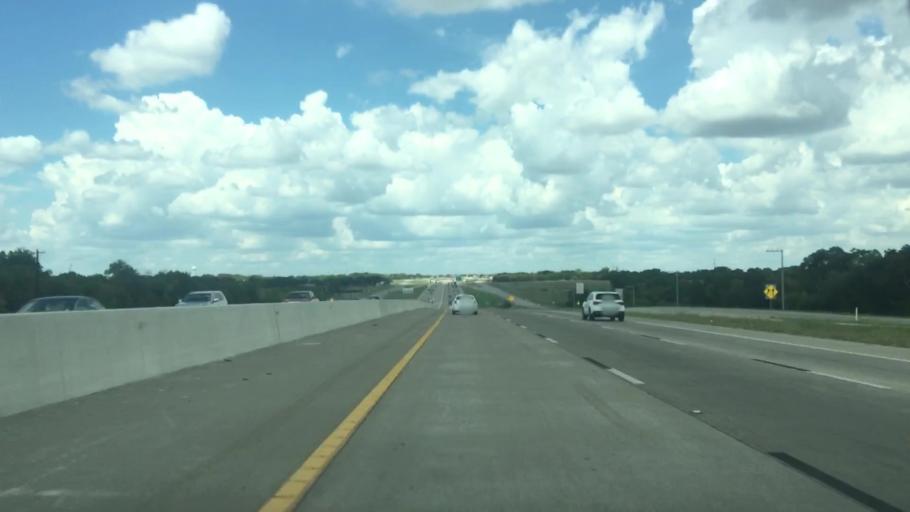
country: US
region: Texas
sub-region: McLennan County
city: Lorena
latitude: 31.3650
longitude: -97.2168
